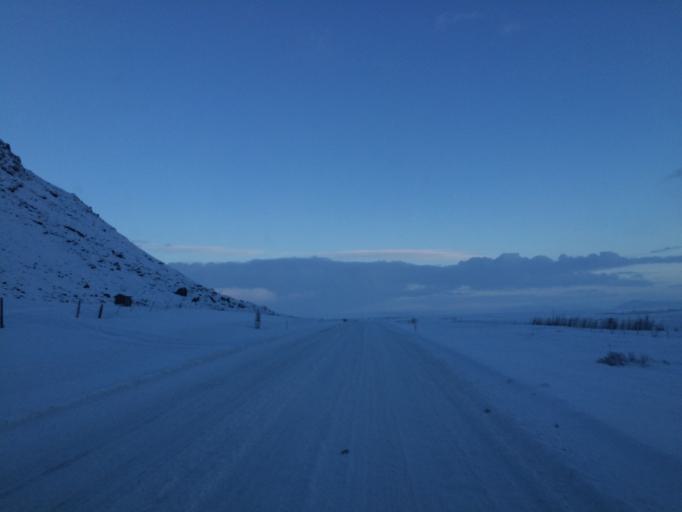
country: IS
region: South
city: Selfoss
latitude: 63.9606
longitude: -21.0061
